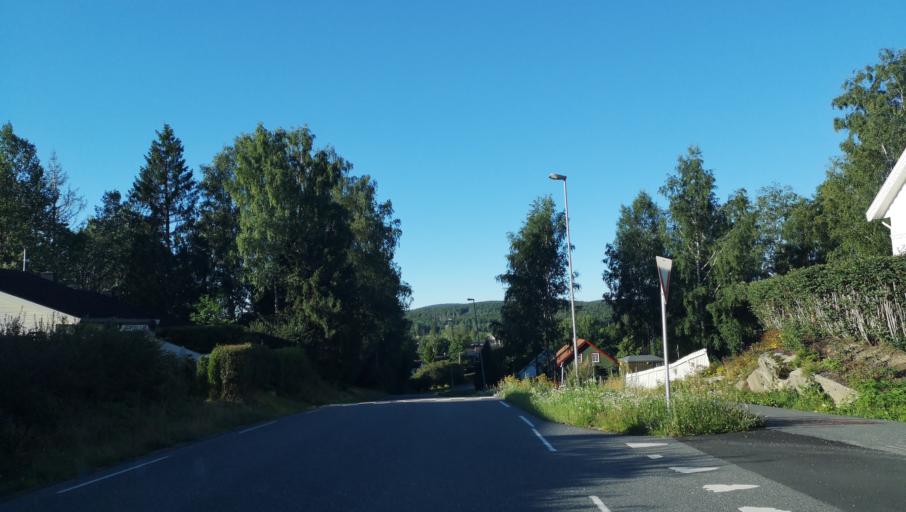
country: NO
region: Ostfold
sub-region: Hobol
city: Knappstad
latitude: 59.6283
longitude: 11.0270
